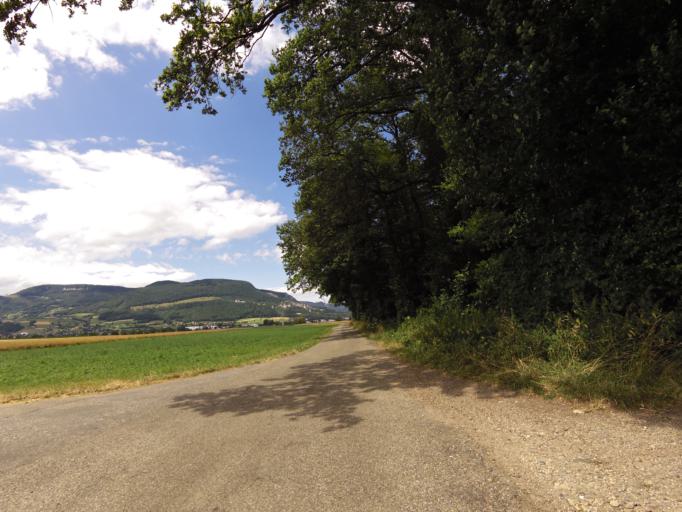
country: CH
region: Solothurn
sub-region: Bezirk Gaeu
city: Oensingen
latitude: 47.2631
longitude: 7.7254
